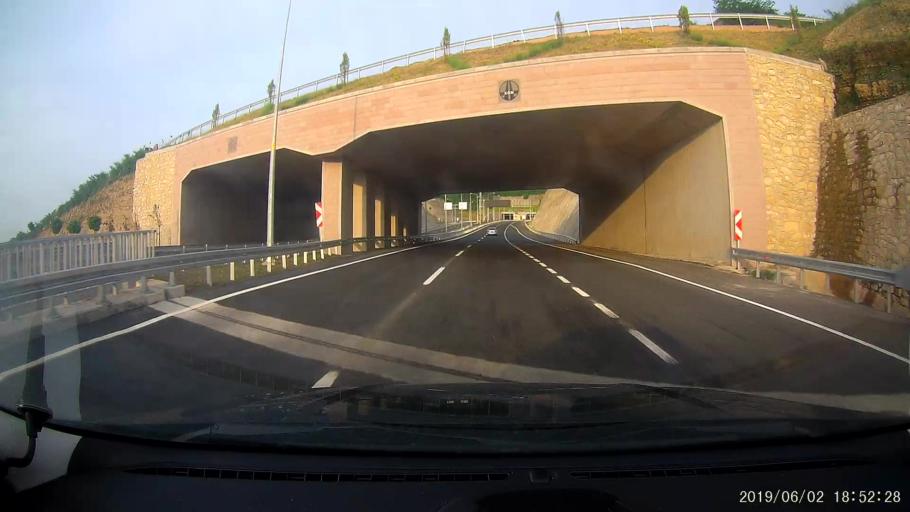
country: TR
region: Ordu
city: Ordu
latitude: 40.9887
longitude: 37.8122
